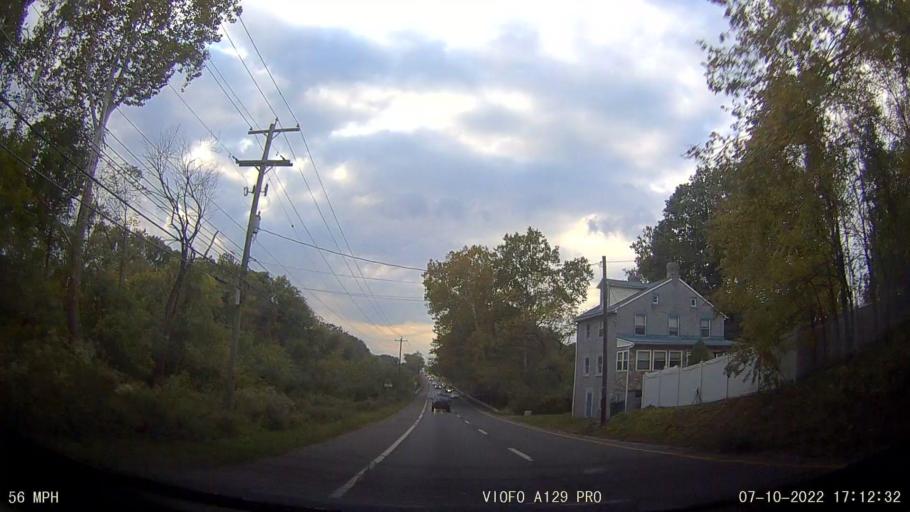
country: US
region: Pennsylvania
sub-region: Berks County
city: Amity Gardens
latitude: 40.2625
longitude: -75.7368
